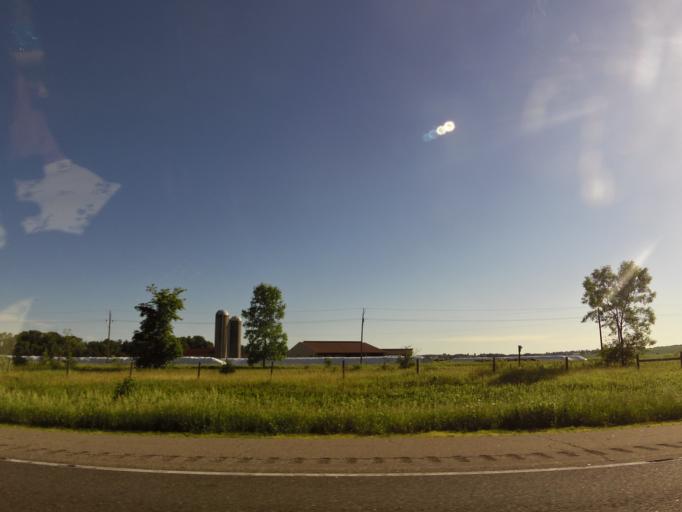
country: US
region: Minnesota
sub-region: Stearns County
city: Albany
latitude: 45.6572
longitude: -94.6765
